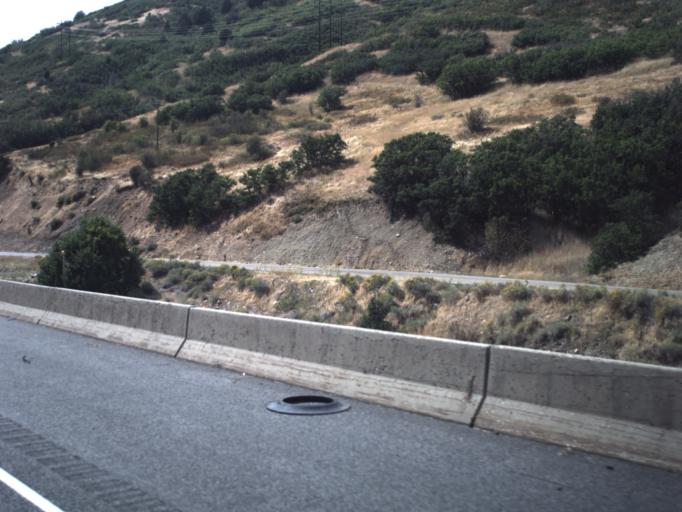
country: US
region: Utah
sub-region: Salt Lake County
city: Mount Olympus
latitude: 40.7465
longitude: -111.7261
